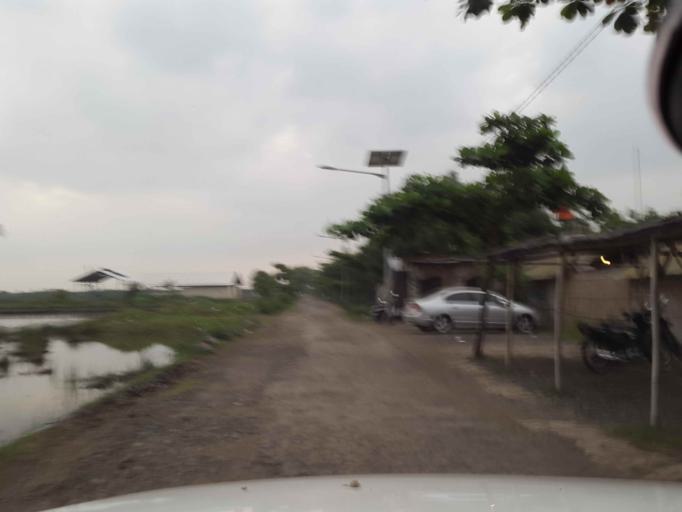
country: ID
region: Central Java
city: Tegal
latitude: -6.8633
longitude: 109.1008
